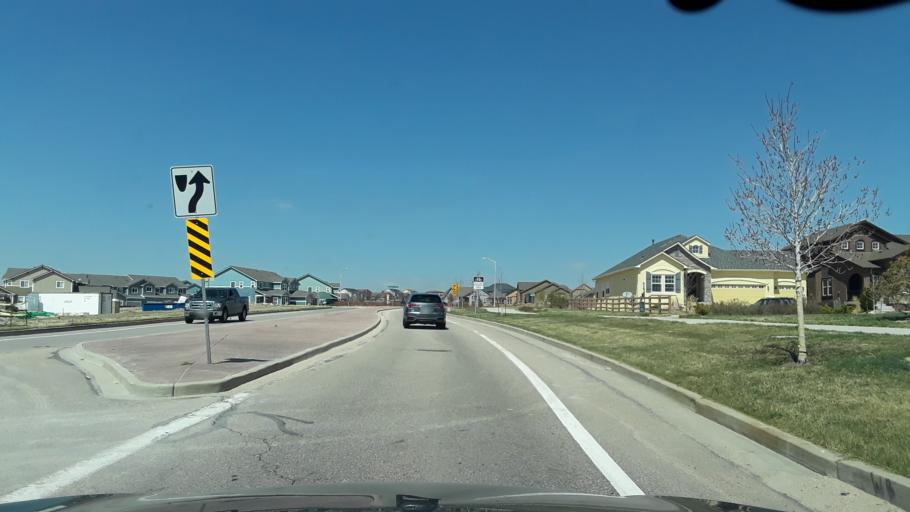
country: US
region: Colorado
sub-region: El Paso County
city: Black Forest
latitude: 38.9591
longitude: -104.7257
